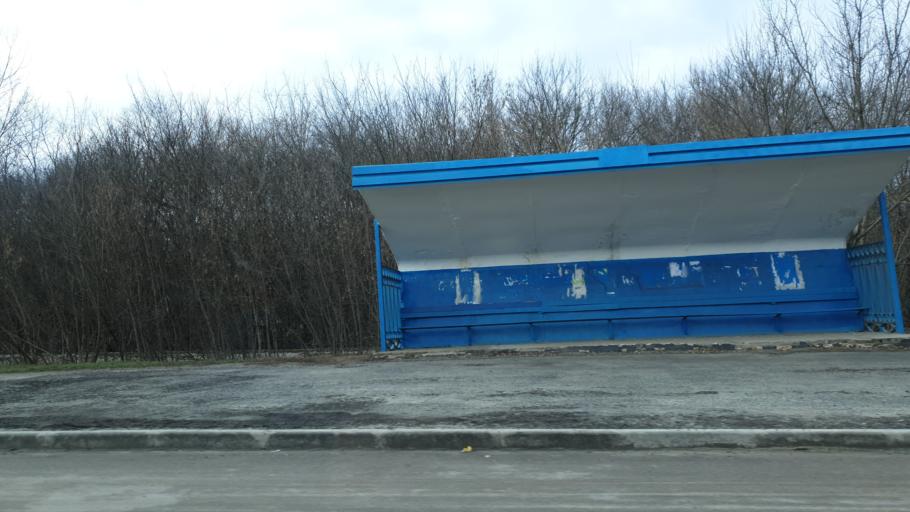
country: RU
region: Kursk
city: Kursk
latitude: 51.6824
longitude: 36.1495
